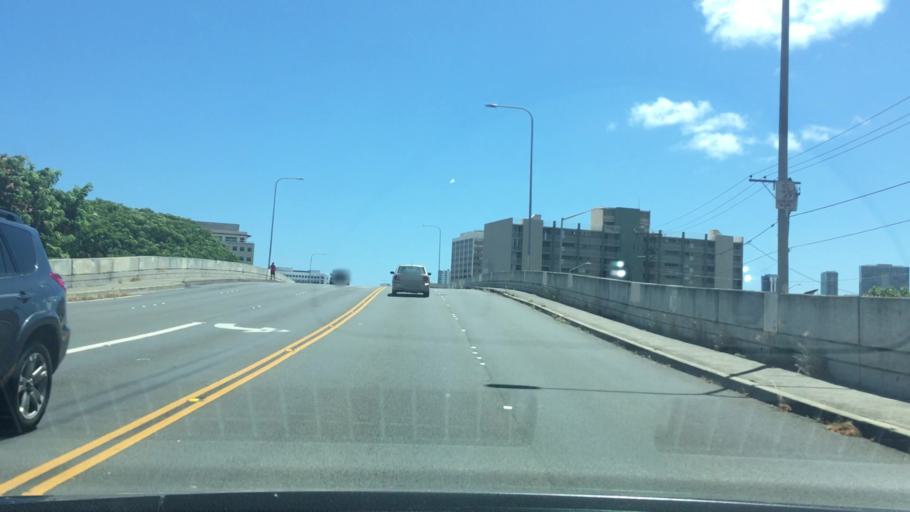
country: US
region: Hawaii
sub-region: Honolulu County
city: Honolulu
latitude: 21.3032
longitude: -157.8378
